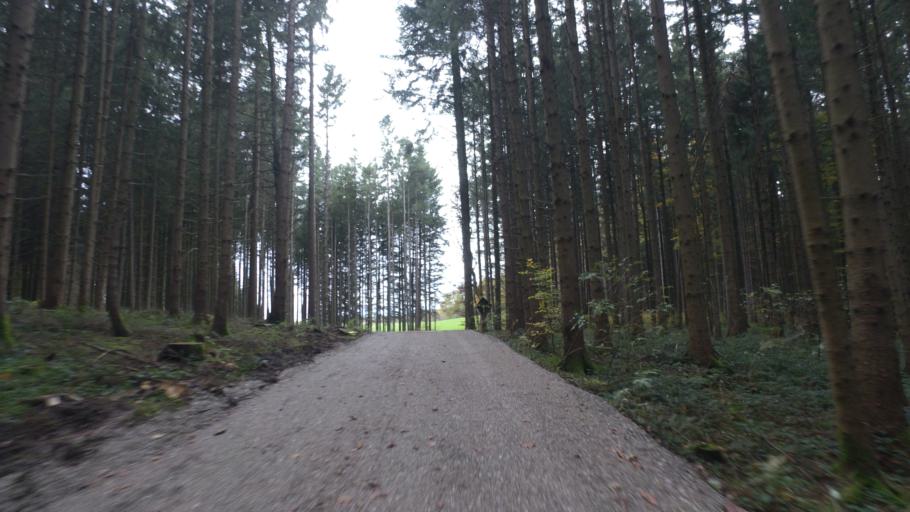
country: DE
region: Bavaria
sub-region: Upper Bavaria
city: Nussdorf
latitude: 47.9107
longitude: 12.5748
